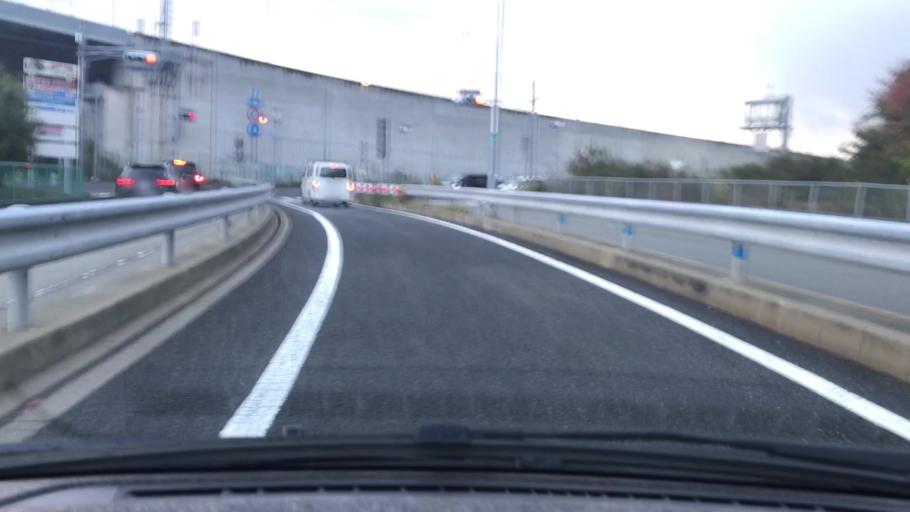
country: JP
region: Hyogo
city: Sandacho
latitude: 34.8340
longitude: 135.2606
